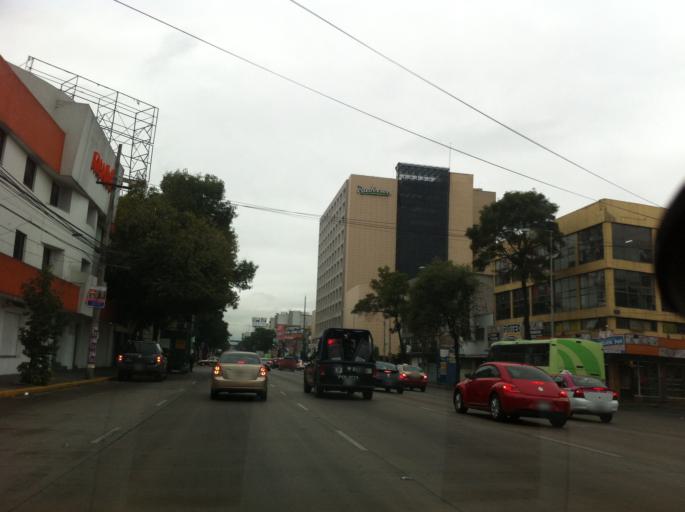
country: MX
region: Mexico City
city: Polanco
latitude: 19.3984
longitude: -99.1849
